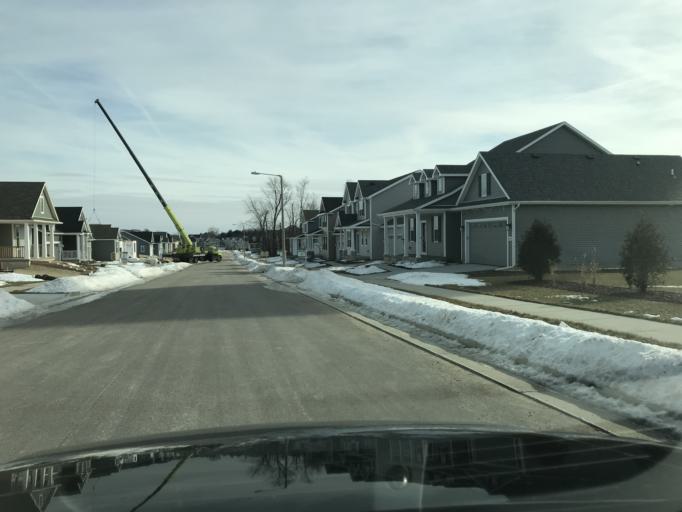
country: US
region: Wisconsin
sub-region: Dane County
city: Monona
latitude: 43.0935
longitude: -89.2786
